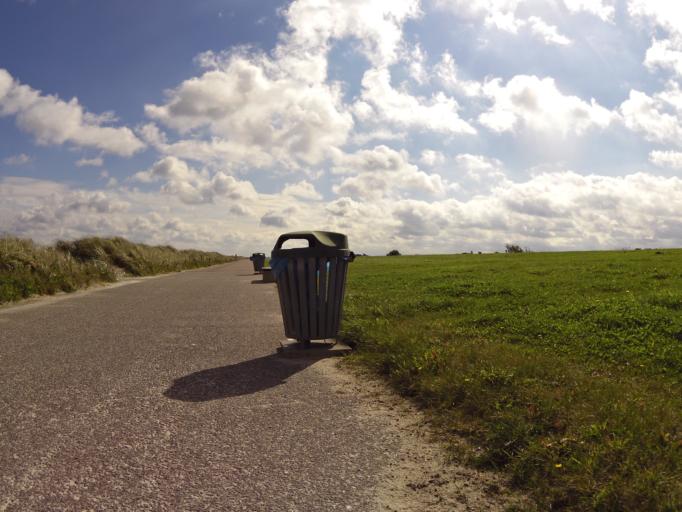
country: DE
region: Schleswig-Holstein
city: Wisch
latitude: 54.4248
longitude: 10.3912
